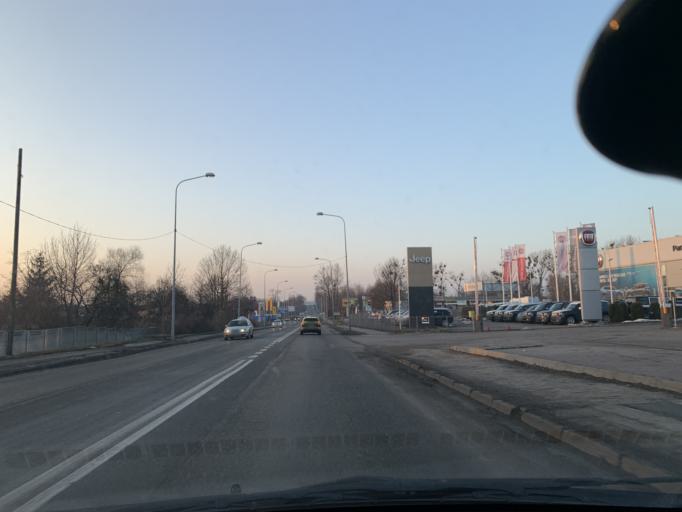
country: PL
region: Silesian Voivodeship
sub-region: Bytom
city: Bytom
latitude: 50.3588
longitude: 18.9061
